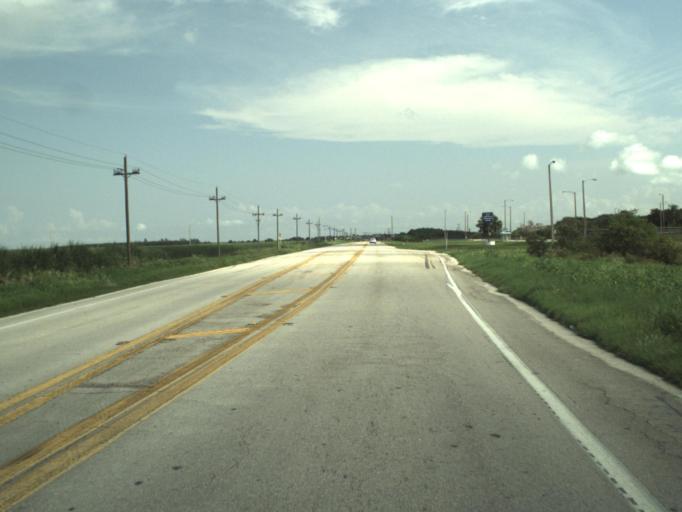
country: US
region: Florida
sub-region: Palm Beach County
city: Belle Glade
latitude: 26.7176
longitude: -80.6840
